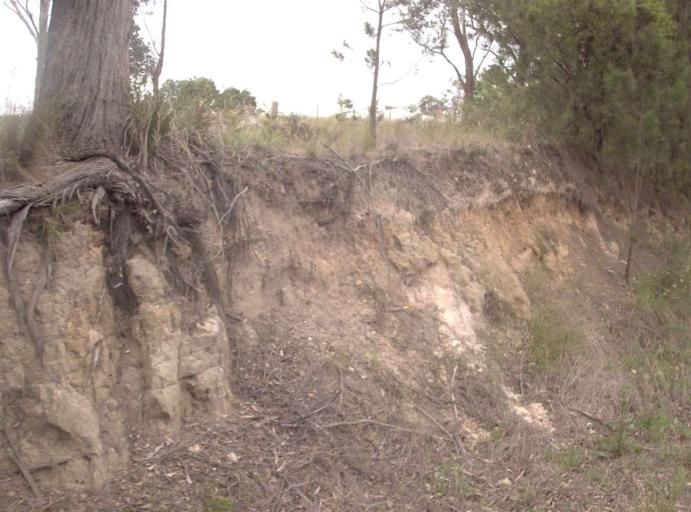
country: AU
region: Victoria
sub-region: East Gippsland
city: Bairnsdale
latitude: -37.7568
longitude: 147.5990
